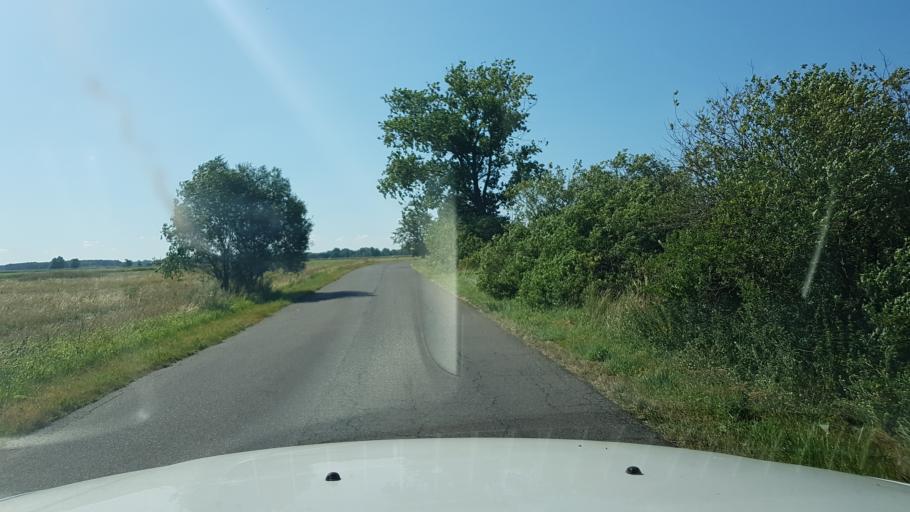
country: PL
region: West Pomeranian Voivodeship
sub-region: Powiat goleniowski
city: Goleniow
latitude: 53.4910
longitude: 14.7125
